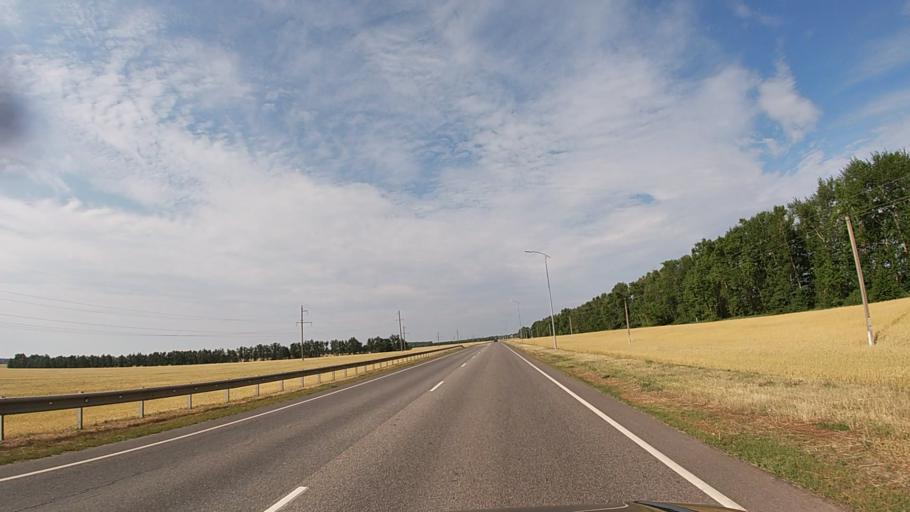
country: RU
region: Belgorod
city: Proletarskiy
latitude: 50.8164
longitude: 35.7526
